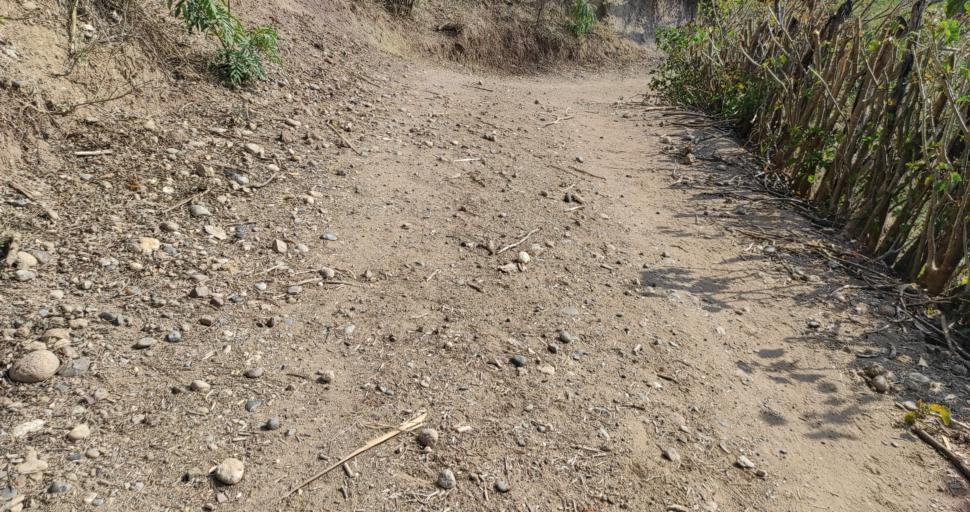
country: EC
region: Loja
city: Catacocha
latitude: -4.0039
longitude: -79.7140
